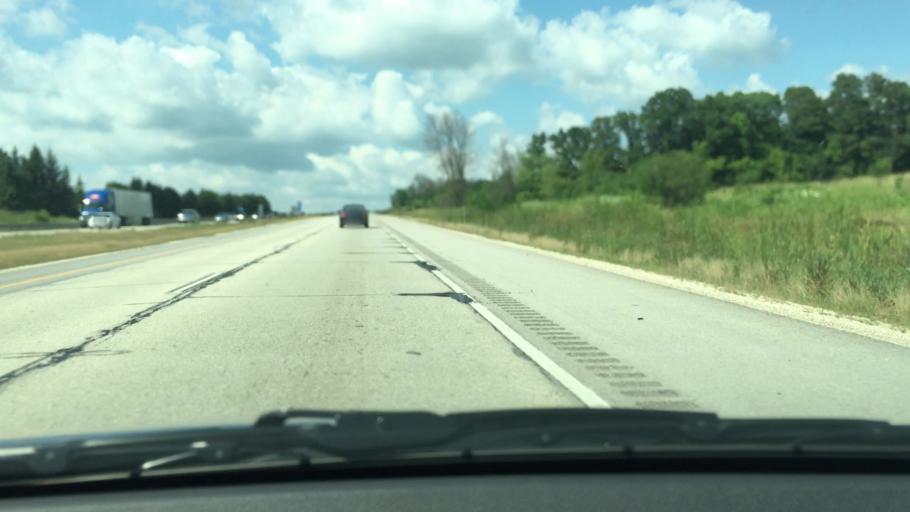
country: US
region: Wisconsin
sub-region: Dodge County
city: Theresa
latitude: 43.4882
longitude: -88.3667
